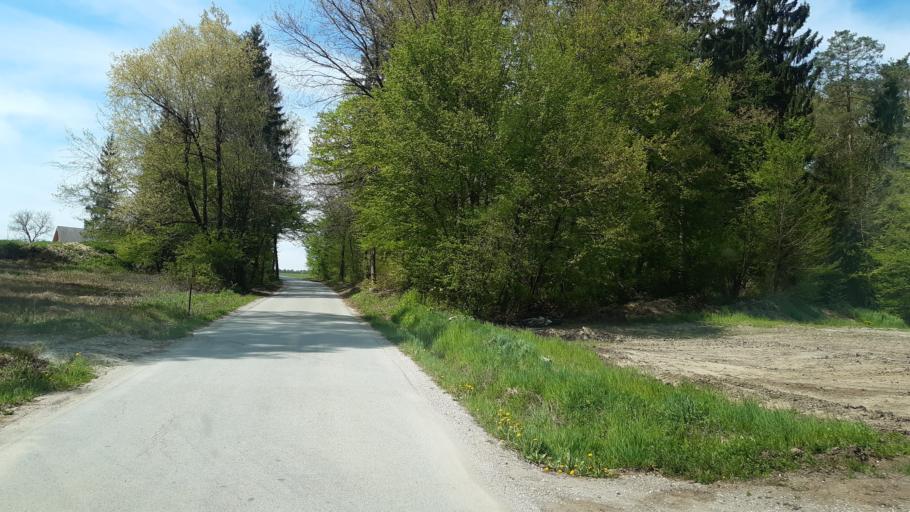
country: SI
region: Domzale
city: Dob
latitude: 46.1765
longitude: 14.6408
